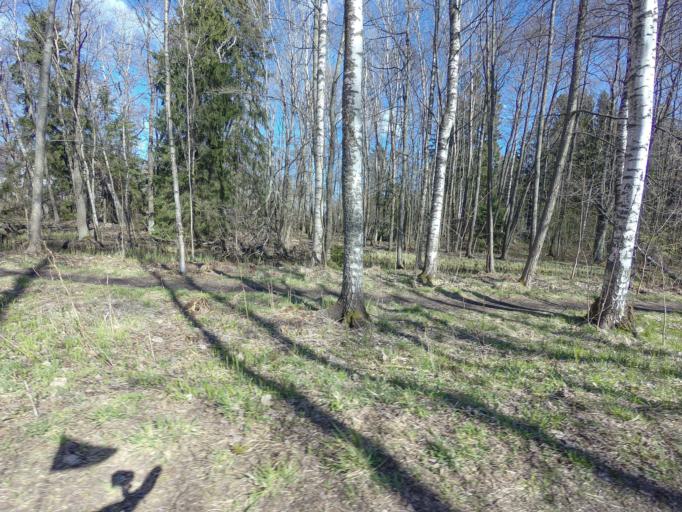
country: FI
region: Uusimaa
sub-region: Helsinki
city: Helsinki
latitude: 60.1724
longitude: 25.0566
